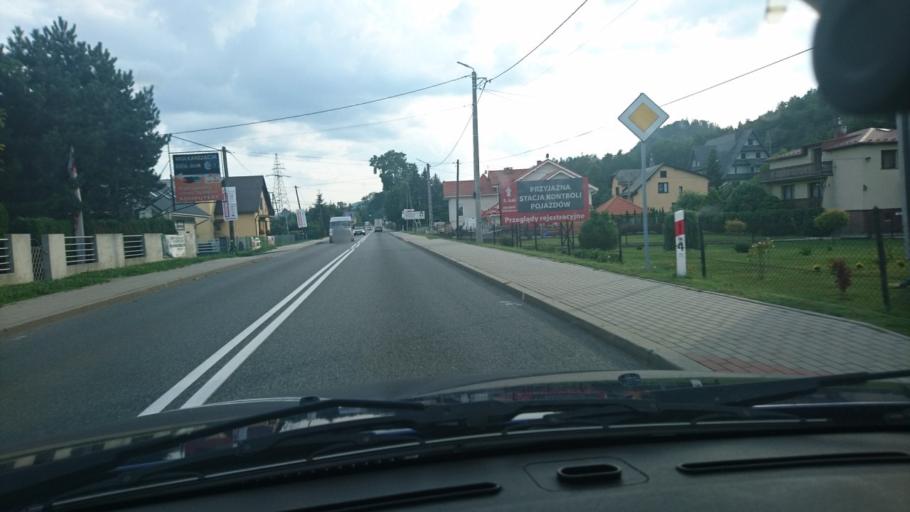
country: PL
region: Silesian Voivodeship
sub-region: Powiat zywiecki
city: Wegierska Gorka
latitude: 49.6129
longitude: 19.1197
